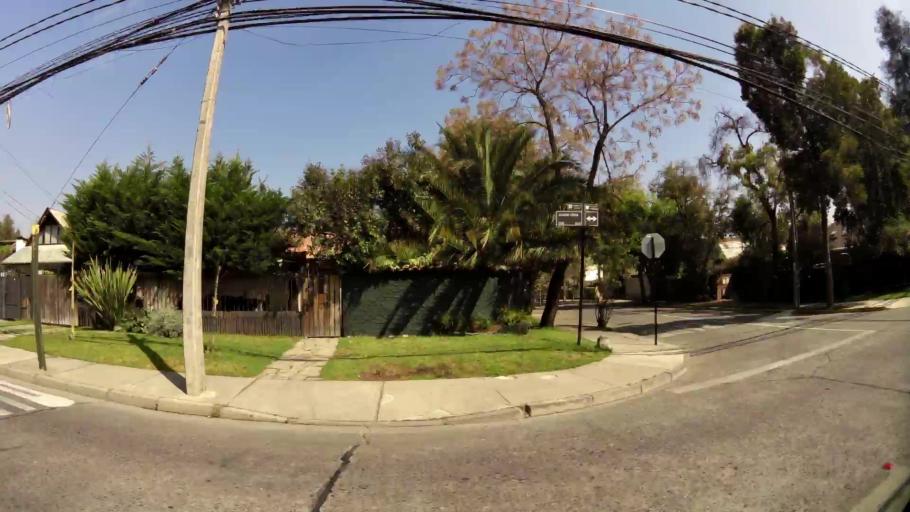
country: CL
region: Santiago Metropolitan
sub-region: Provincia de Santiago
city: Villa Presidente Frei, Nunoa, Santiago, Chile
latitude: -33.3852
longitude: -70.5726
